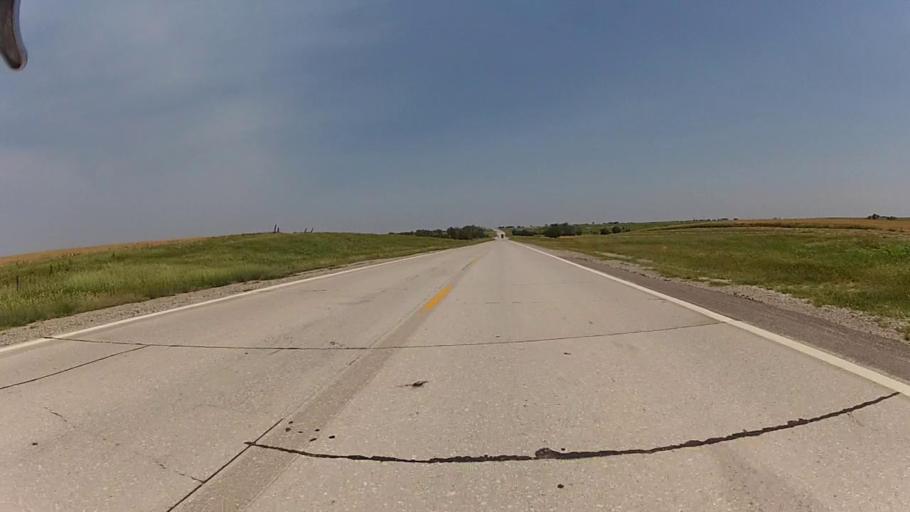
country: US
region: Kansas
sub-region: Sumner County
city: Wellington
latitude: 37.0577
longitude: -97.3523
